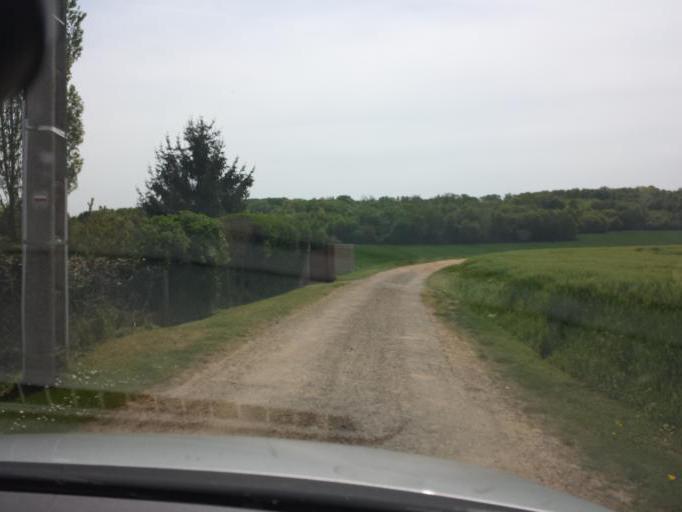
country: FR
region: Centre
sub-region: Departement d'Eure-et-Loir
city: Oulins
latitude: 48.8433
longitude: 1.4636
